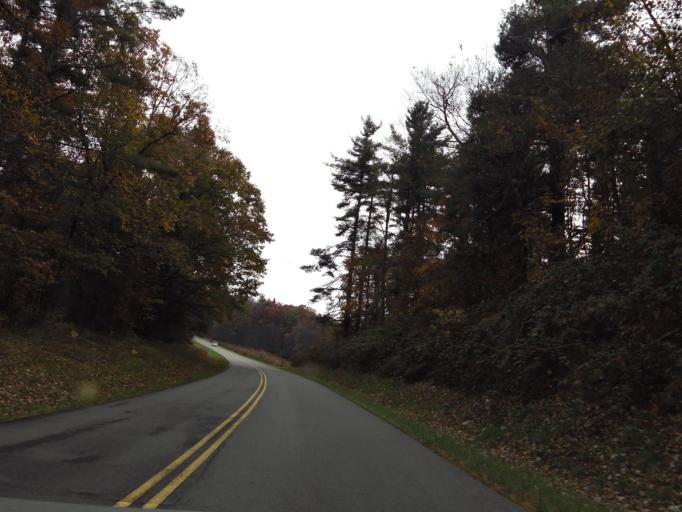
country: US
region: North Carolina
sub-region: Ashe County
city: Jefferson
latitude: 36.3341
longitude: -81.3746
